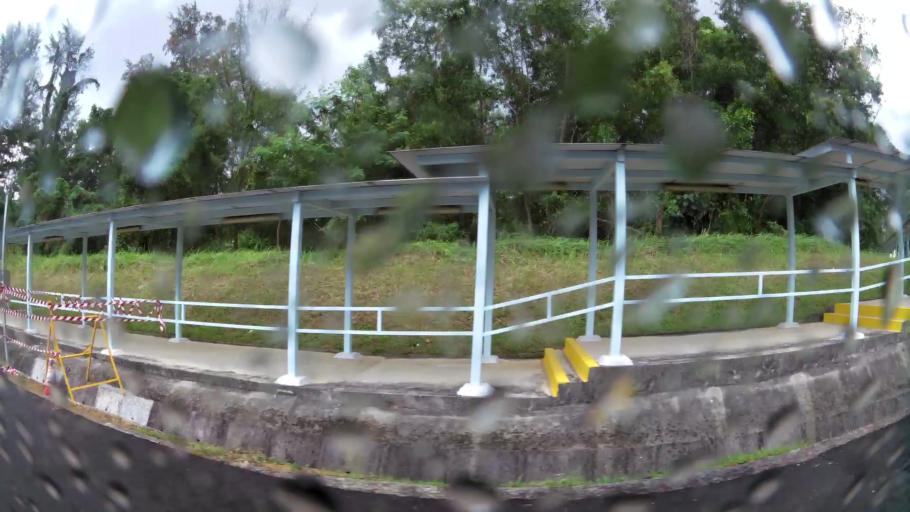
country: MY
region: Johor
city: Kampung Pasir Gudang Baru
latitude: 1.4096
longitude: 103.8686
